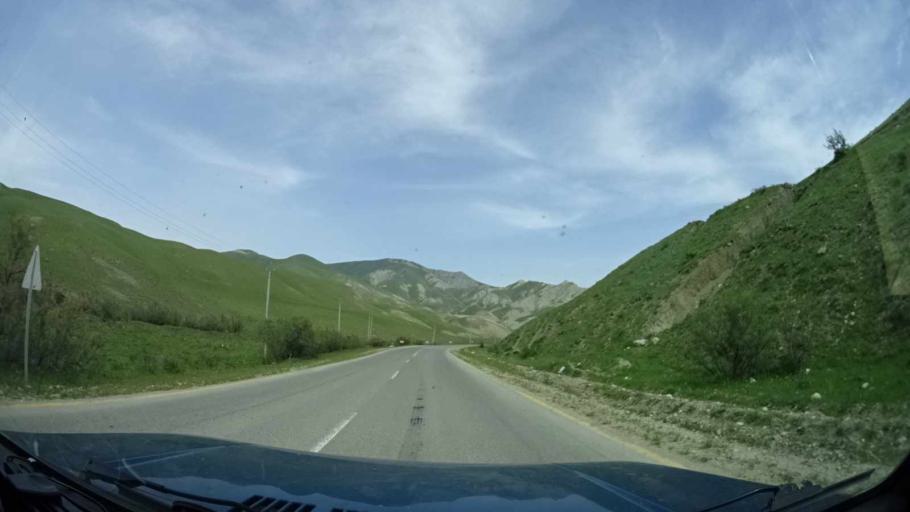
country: AZ
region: Xizi
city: Khyzy
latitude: 40.9082
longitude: 49.1270
